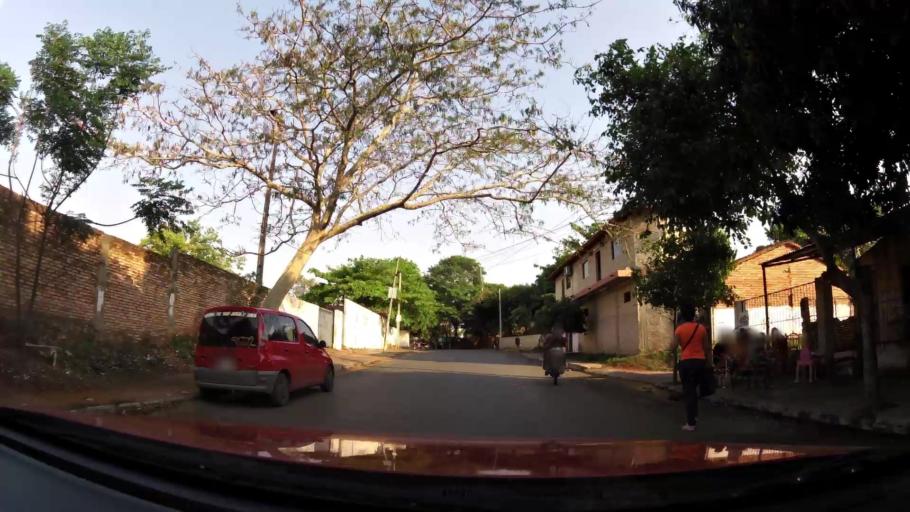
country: PY
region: Central
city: Lambare
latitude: -25.3520
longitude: -57.5971
